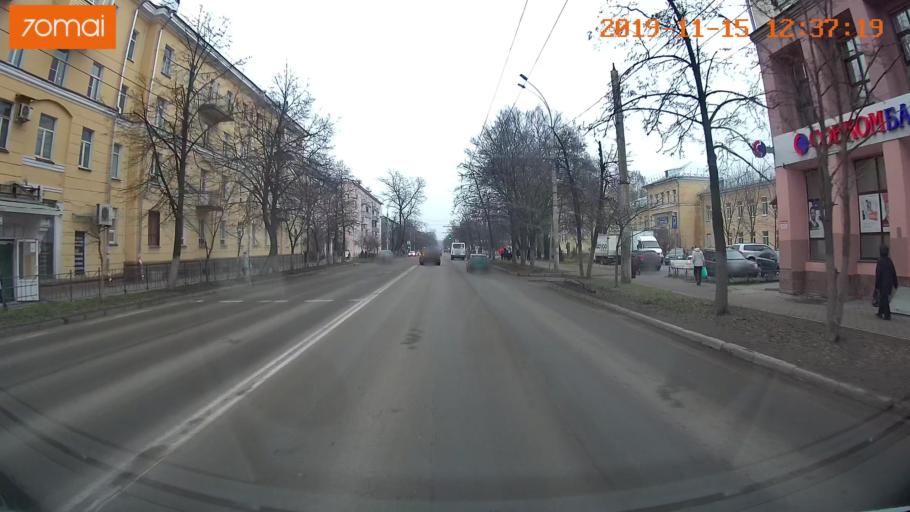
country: RU
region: Vologda
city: Vologda
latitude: 59.2099
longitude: 39.8975
